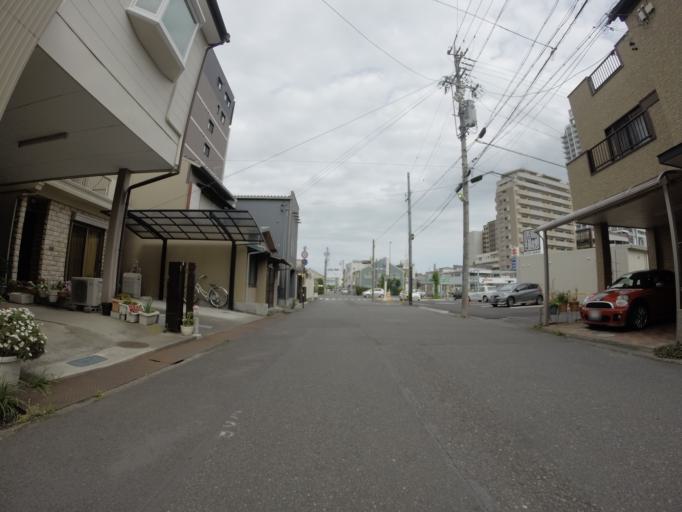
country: JP
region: Shizuoka
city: Shizuoka-shi
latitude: 35.0256
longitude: 138.4868
